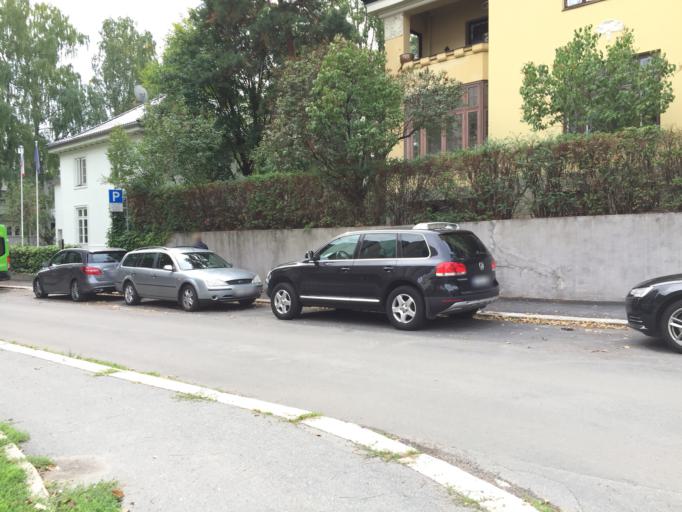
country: NO
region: Oslo
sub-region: Oslo
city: Sjolyststranda
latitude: 59.9171
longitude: 10.7053
